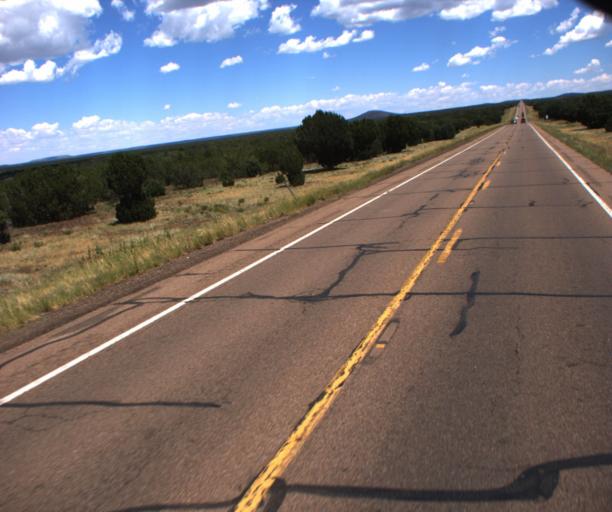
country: US
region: Arizona
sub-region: Navajo County
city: Show Low
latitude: 34.2649
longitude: -109.9572
